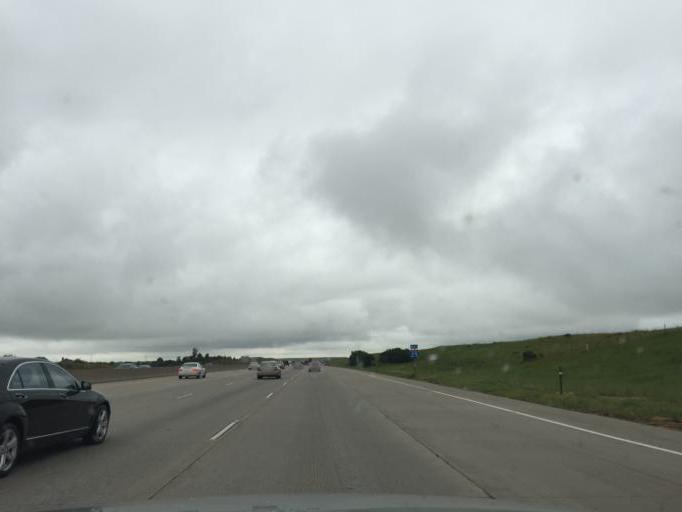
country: US
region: Colorado
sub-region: Park County
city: Castle Pines North
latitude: 39.4777
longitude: -104.8723
